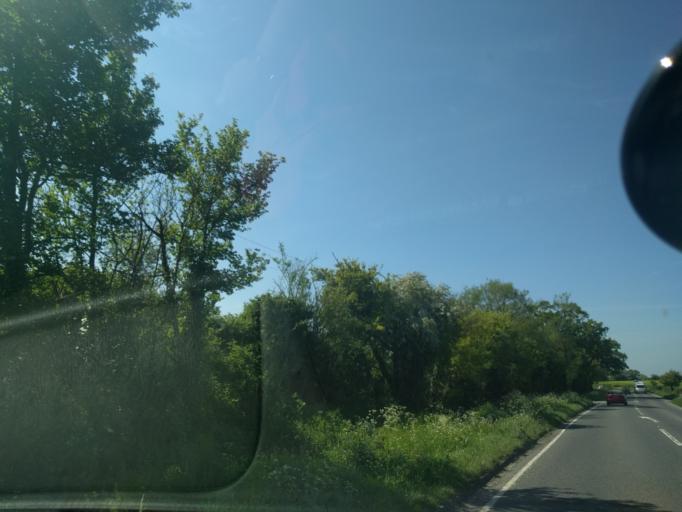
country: GB
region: England
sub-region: Somerset
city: Ilchester
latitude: 51.0711
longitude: -2.6251
